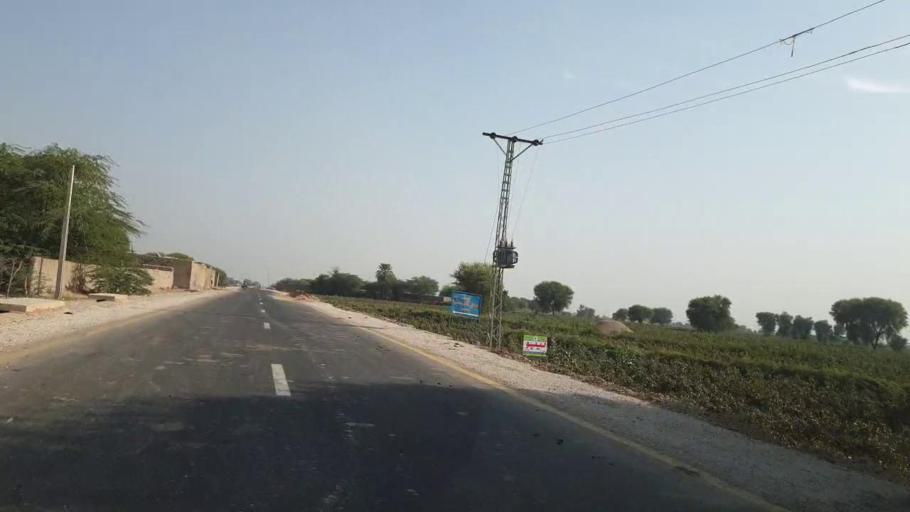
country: PK
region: Sindh
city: Sehwan
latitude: 26.4806
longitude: 67.7819
